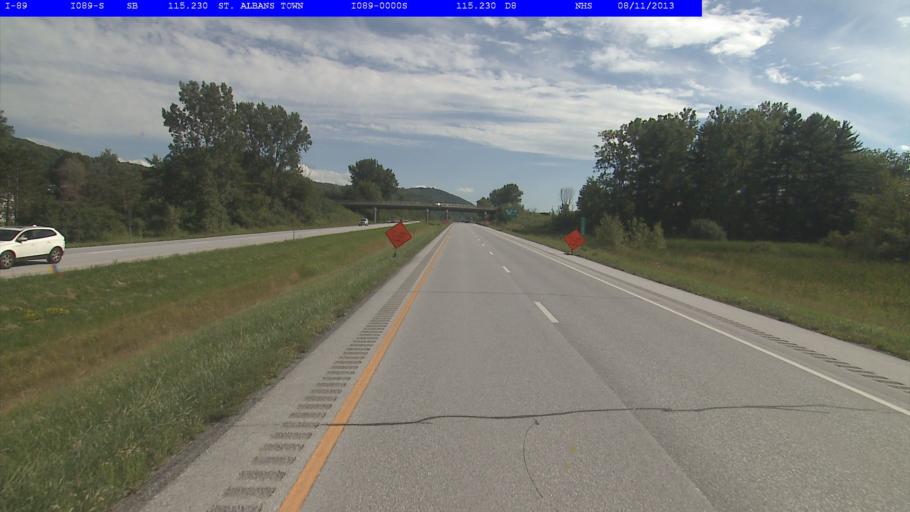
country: US
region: Vermont
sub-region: Franklin County
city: Saint Albans
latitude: 44.8157
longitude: -73.0636
